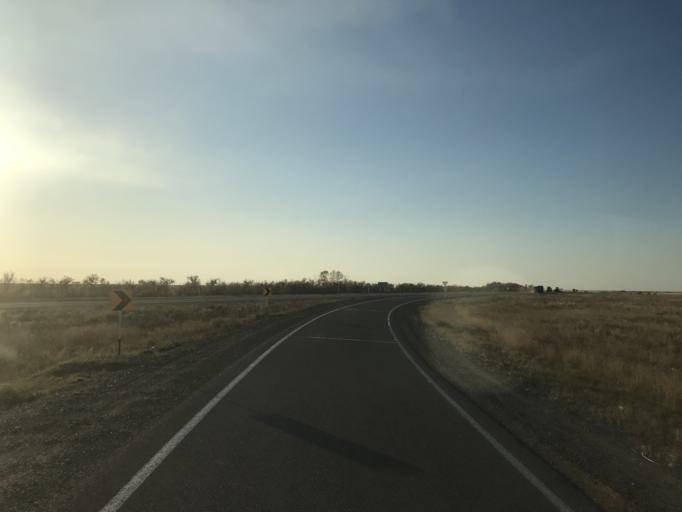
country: KZ
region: Pavlodar
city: Leninskiy
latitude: 52.1551
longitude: 76.8196
